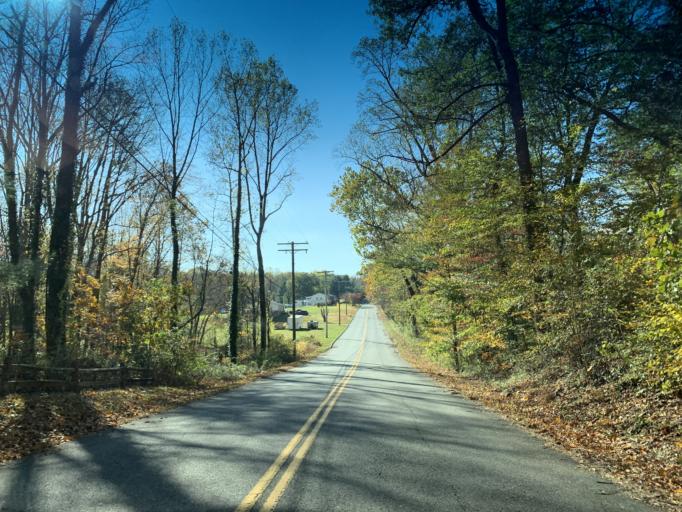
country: US
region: Maryland
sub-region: Harford County
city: Joppatowne
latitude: 39.4731
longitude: -76.3675
